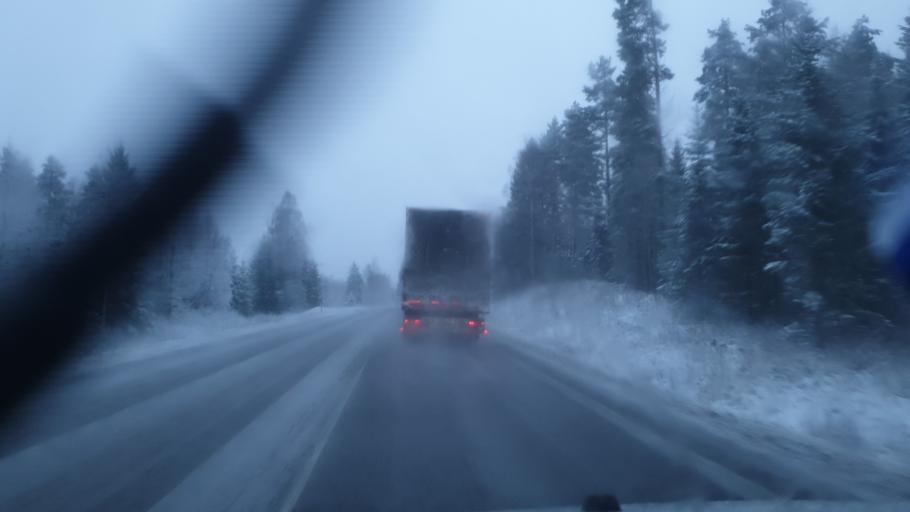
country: FI
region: Central Finland
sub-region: Saarijaervi-Viitasaari
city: Viitasaari
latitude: 62.9171
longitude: 25.8191
